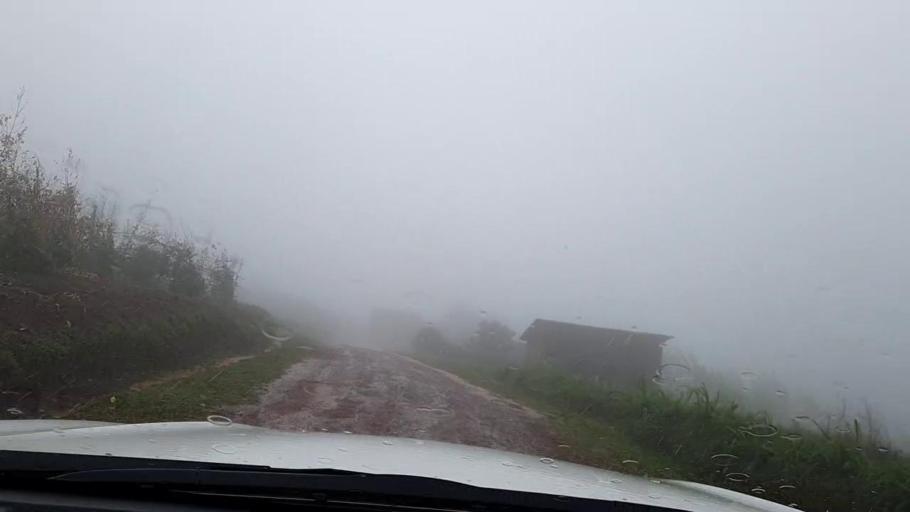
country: RW
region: Northern Province
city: Byumba
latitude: -1.7311
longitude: 30.0165
